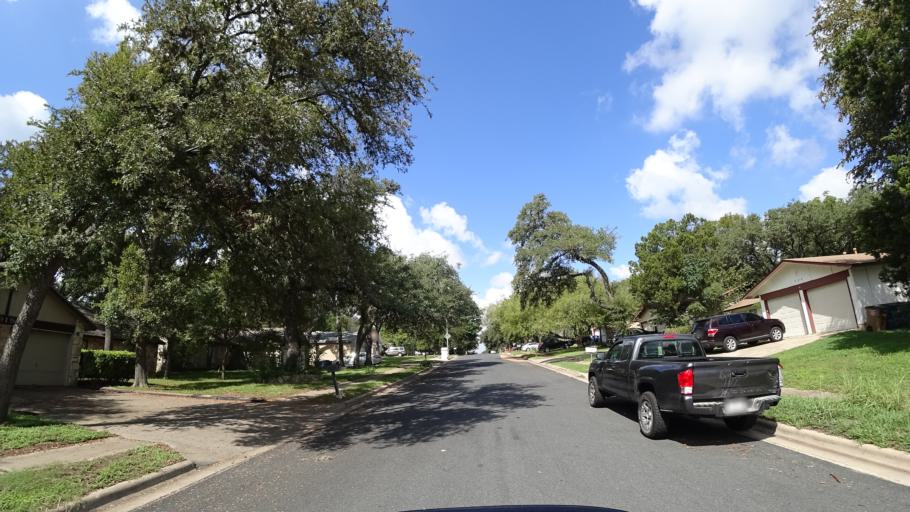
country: US
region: Texas
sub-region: Travis County
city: Onion Creek
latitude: 30.1973
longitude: -97.7930
